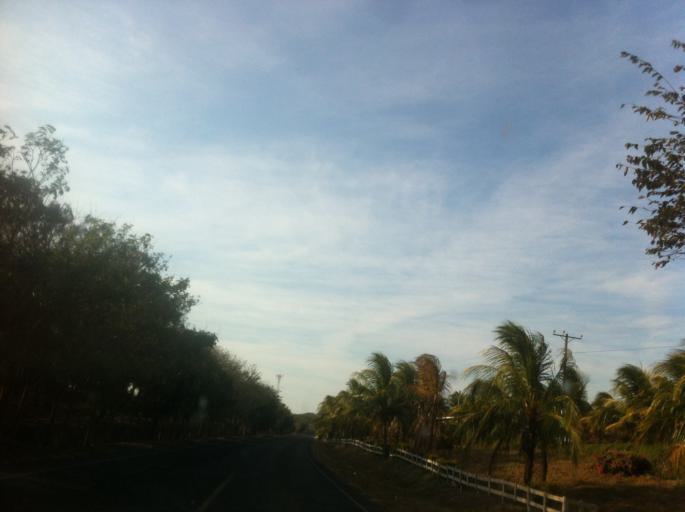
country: NI
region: Rivas
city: San Juan del Sur
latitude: 11.2935
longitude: -85.6835
